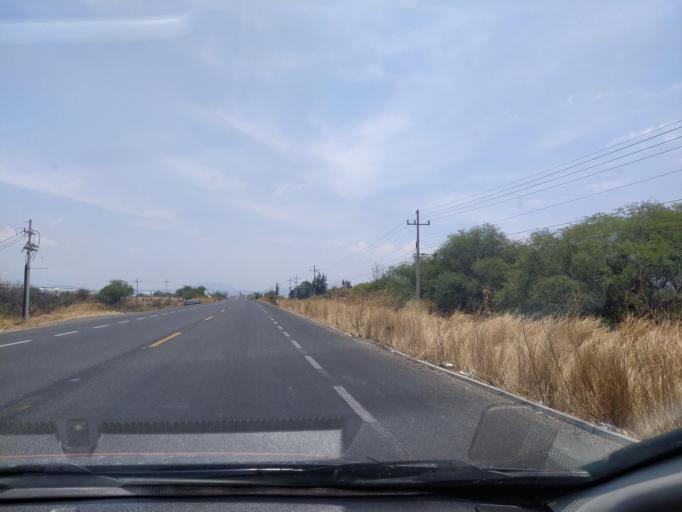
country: MX
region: Jalisco
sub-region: Acatlan de Juarez
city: Villa de los Ninos
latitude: 20.3344
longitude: -103.5908
